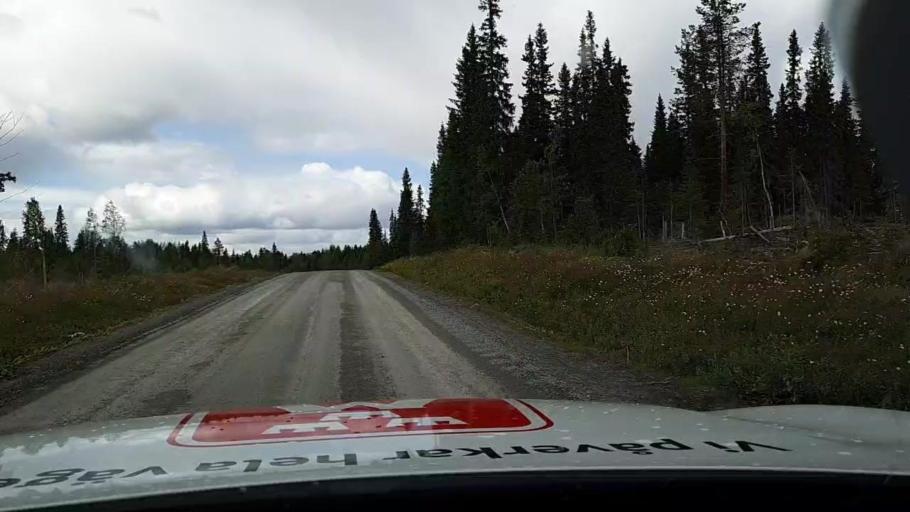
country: SE
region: Jaemtland
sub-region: Krokoms Kommun
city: Valla
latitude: 63.6594
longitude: 13.7597
